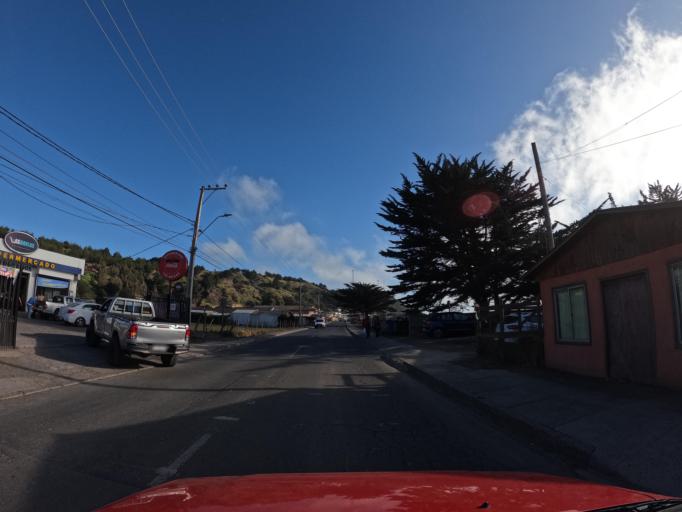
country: CL
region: Maule
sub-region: Provincia de Talca
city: Constitucion
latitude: -34.9345
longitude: -72.1807
